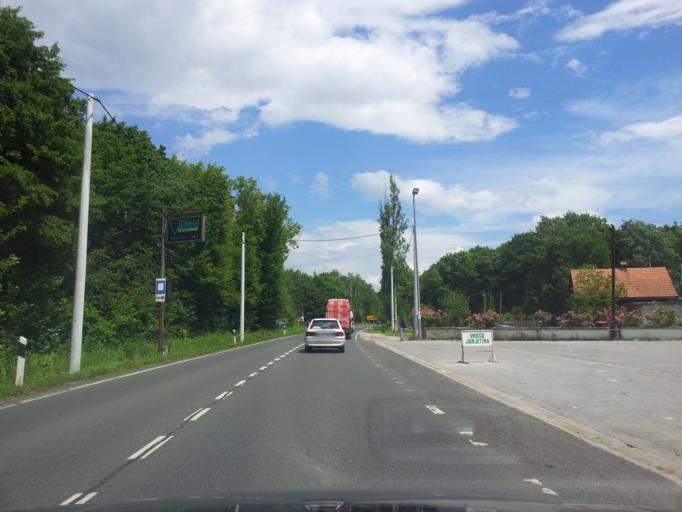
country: HR
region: Grad Zagreb
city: Horvati
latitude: 45.7208
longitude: 15.7809
